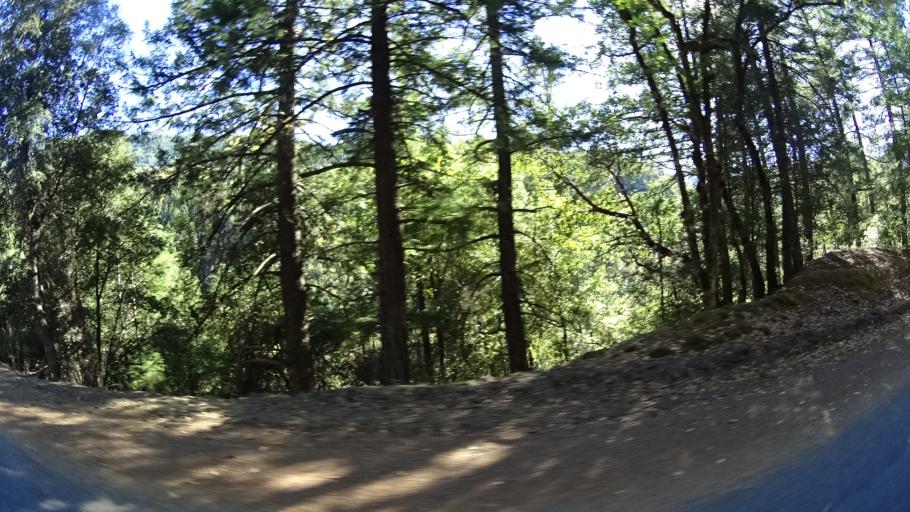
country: US
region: California
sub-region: Humboldt County
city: Willow Creek
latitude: 41.2728
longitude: -123.2972
